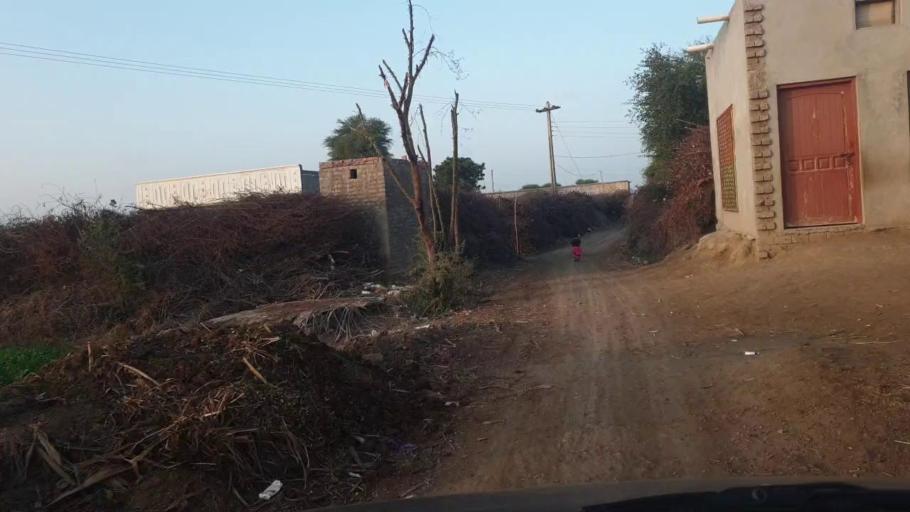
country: PK
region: Sindh
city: Berani
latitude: 25.8525
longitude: 68.7505
